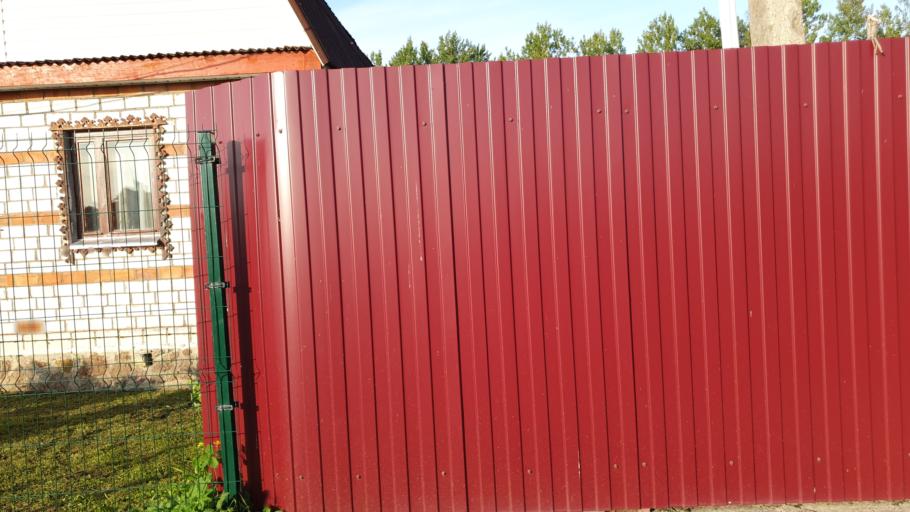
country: RU
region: Leningrad
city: Ivangorod
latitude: 59.4266
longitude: 28.3286
